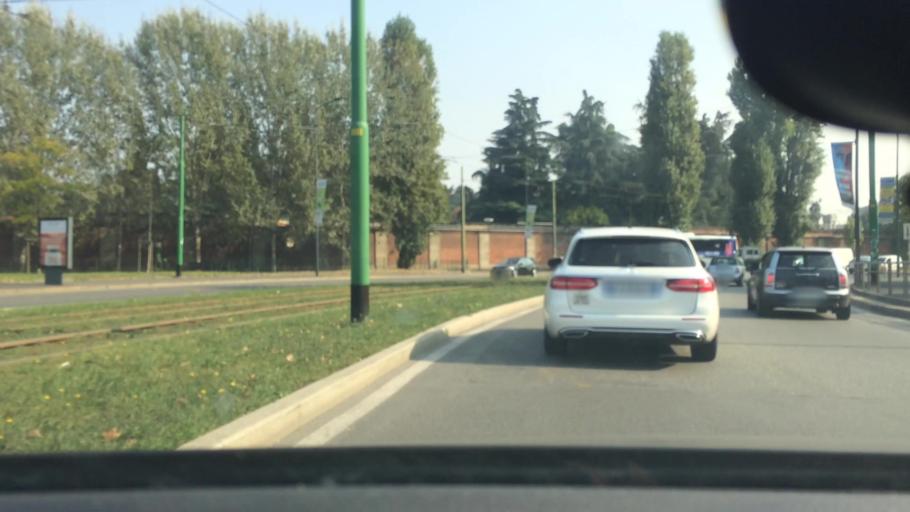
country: IT
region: Lombardy
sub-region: Citta metropolitana di Milano
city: Milano
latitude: 45.4874
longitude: 9.1739
